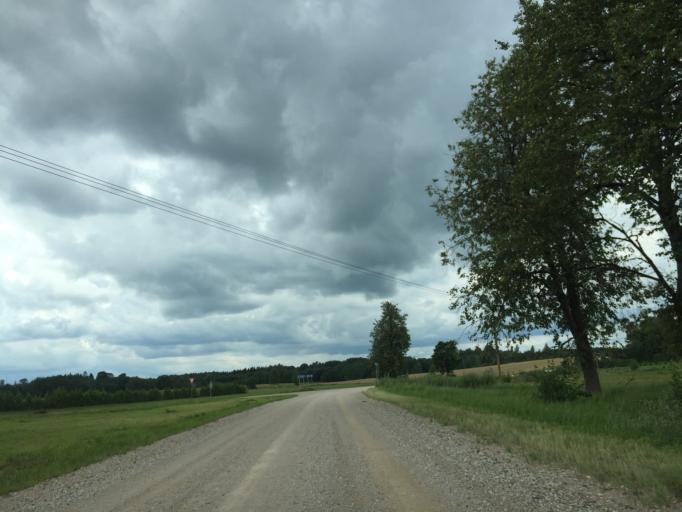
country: LV
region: Malpils
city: Malpils
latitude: 56.8606
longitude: 25.0191
